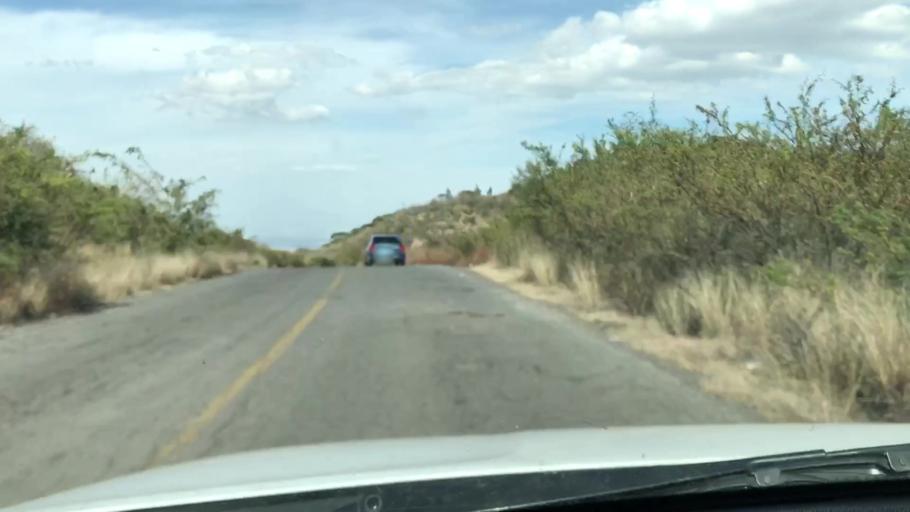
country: MX
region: Jalisco
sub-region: Zacoalco de Torres
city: Barranca de Otates (Barranca de Otatan)
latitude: 20.2452
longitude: -103.6787
